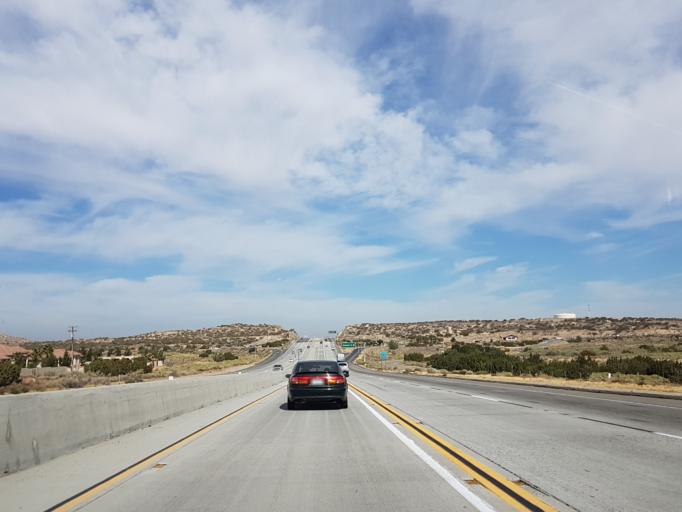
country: US
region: California
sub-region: Los Angeles County
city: Palmdale
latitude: 34.5520
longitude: -118.1318
